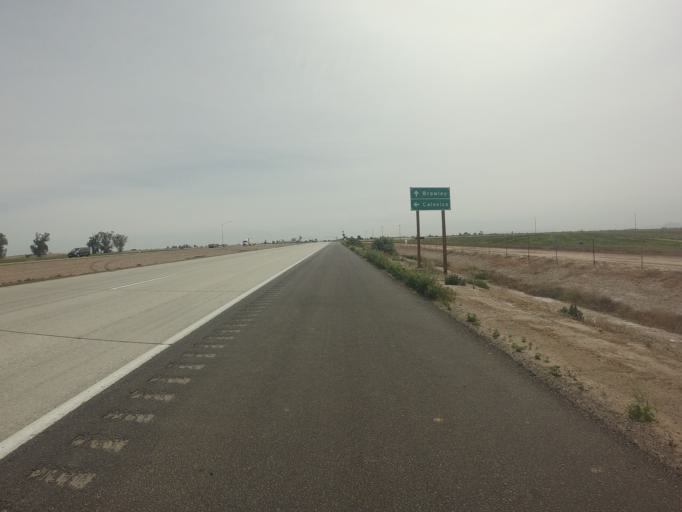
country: US
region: California
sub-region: Imperial County
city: Westmorland
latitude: 33.0035
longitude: -115.5925
